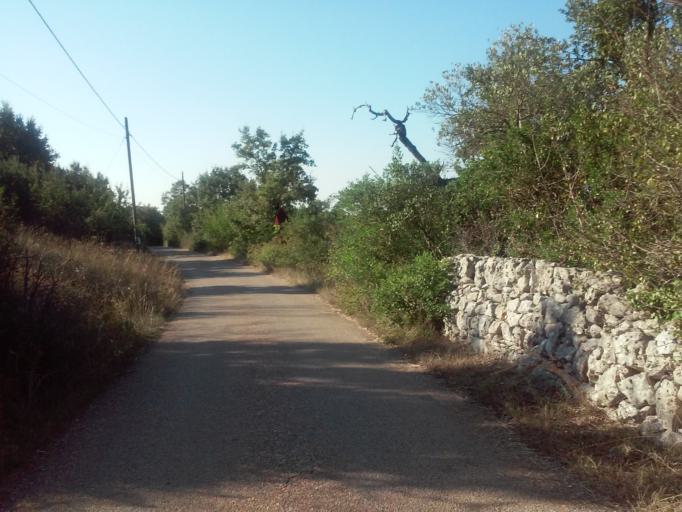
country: IT
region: Apulia
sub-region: Provincia di Bari
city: Noci
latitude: 40.8202
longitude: 17.1504
